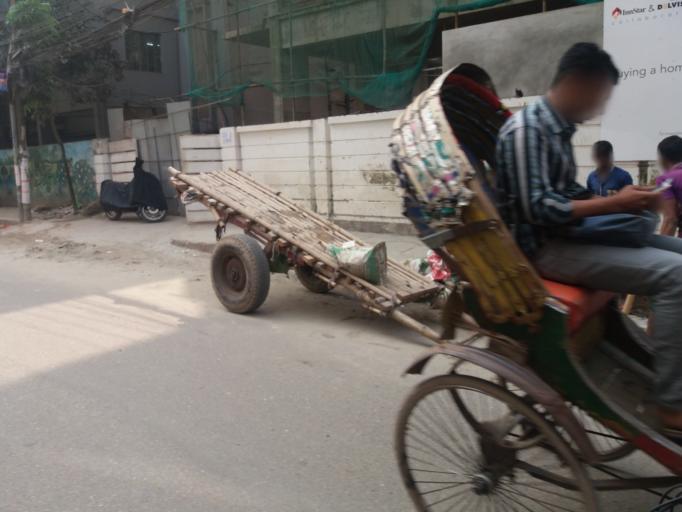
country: BD
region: Dhaka
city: Azimpur
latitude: 23.7463
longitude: 90.3702
